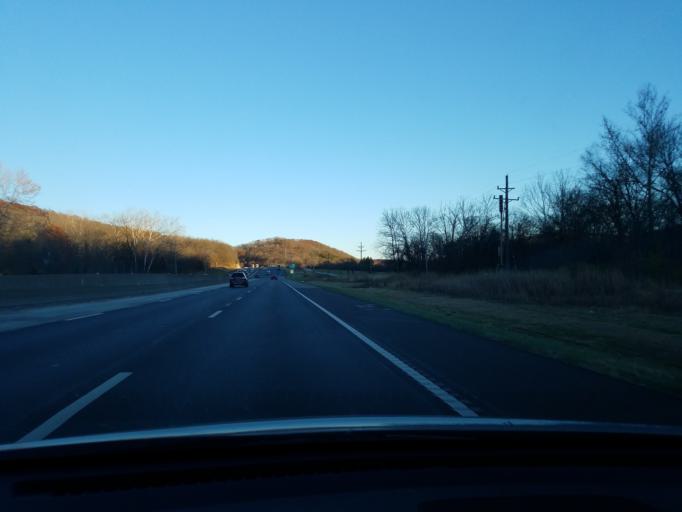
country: US
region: Missouri
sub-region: Jefferson County
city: High Ridge
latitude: 38.5076
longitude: -90.5690
